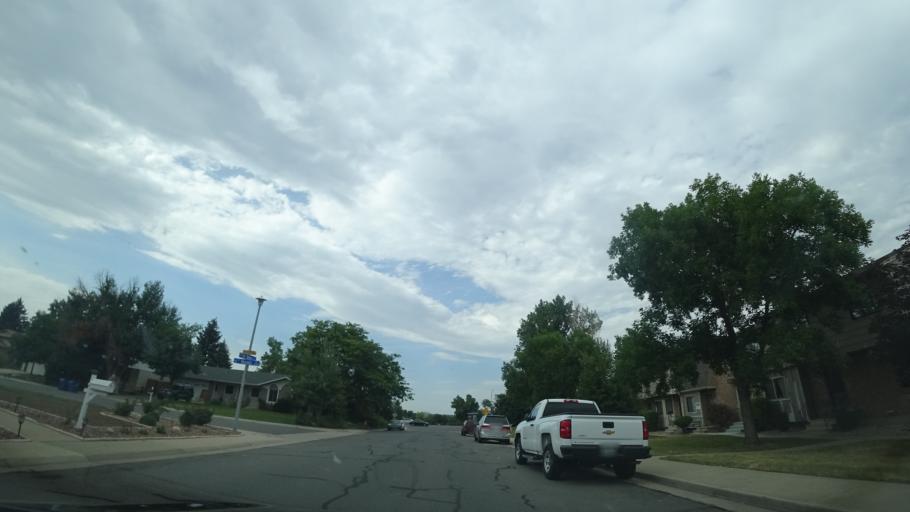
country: US
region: Colorado
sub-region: Jefferson County
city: Lakewood
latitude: 39.7101
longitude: -105.0889
